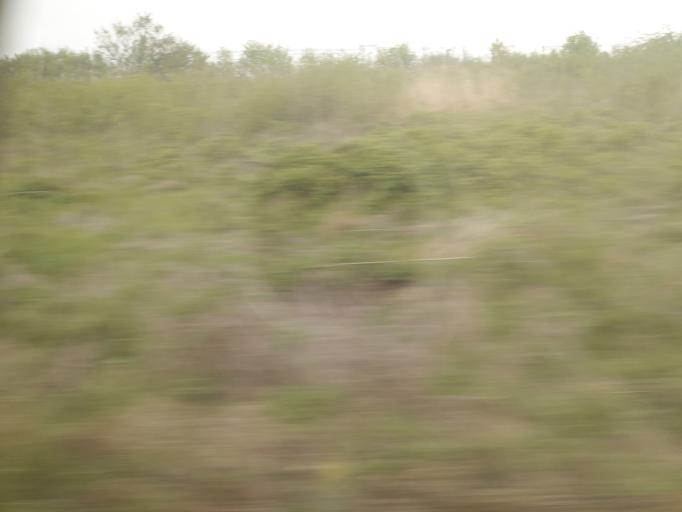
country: FR
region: Ile-de-France
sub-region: Departement du Val-de-Marne
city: Valenton
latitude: 48.7507
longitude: 2.4713
